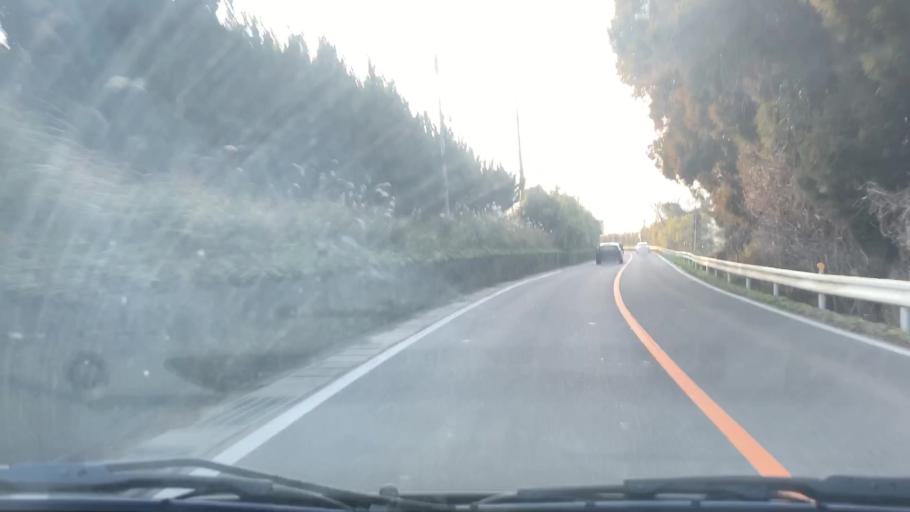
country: JP
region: Saga Prefecture
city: Takeocho-takeo
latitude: 33.2703
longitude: 130.1099
